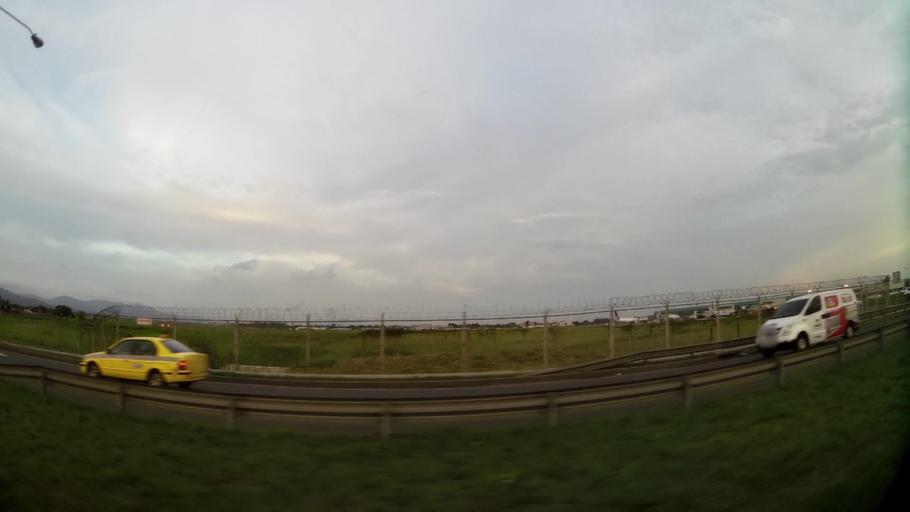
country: PA
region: Panama
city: Tocumen
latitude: 9.0718
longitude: -79.3890
